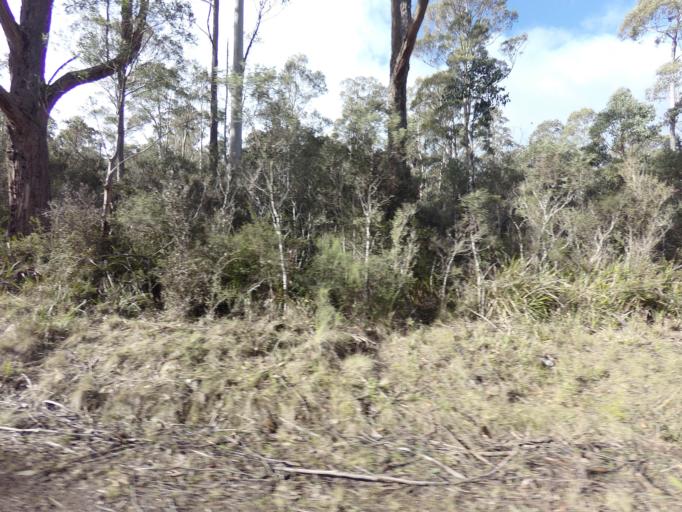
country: AU
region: Tasmania
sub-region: Derwent Valley
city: New Norfolk
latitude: -42.7750
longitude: 146.8991
